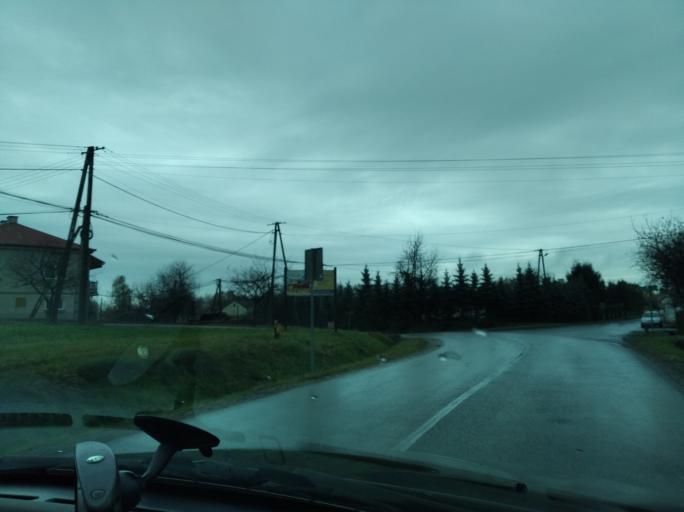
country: PL
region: Subcarpathian Voivodeship
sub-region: Powiat rzeszowski
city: Tyczyn
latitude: 49.9265
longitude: 22.0281
